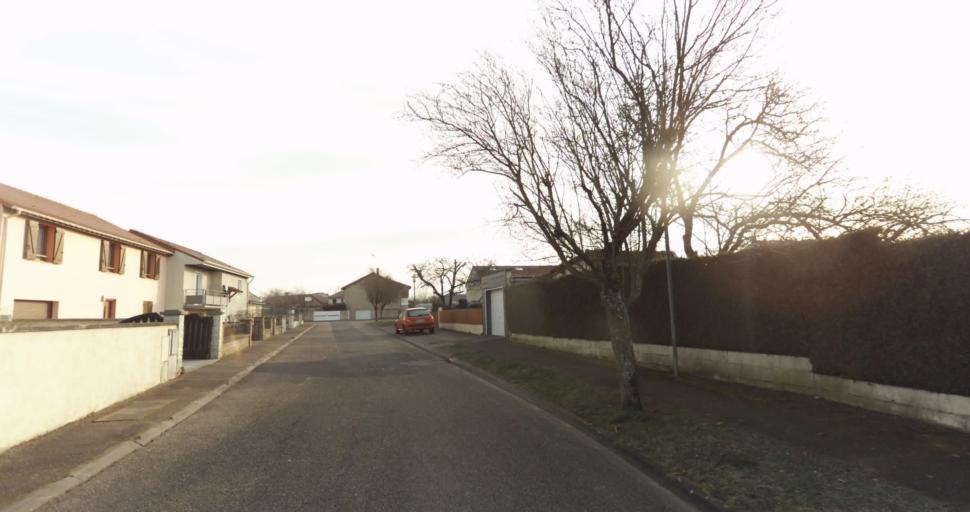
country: FR
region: Lorraine
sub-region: Departement de Meurthe-et-Moselle
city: Labry
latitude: 49.1656
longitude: 5.8856
